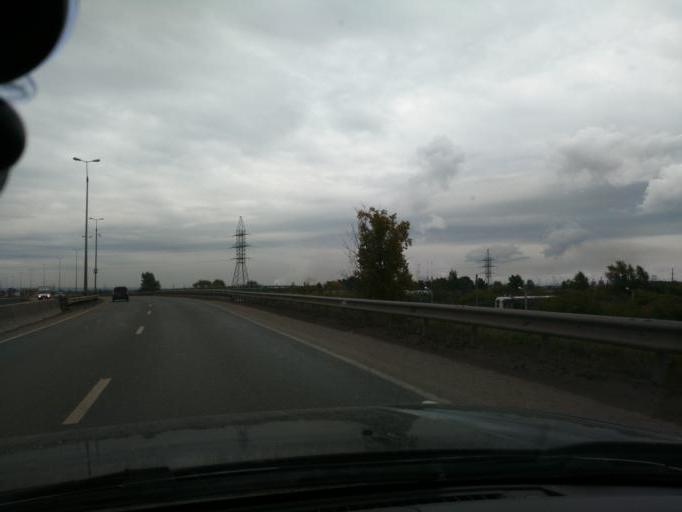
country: RU
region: Perm
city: Kondratovo
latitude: 57.9453
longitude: 56.1261
